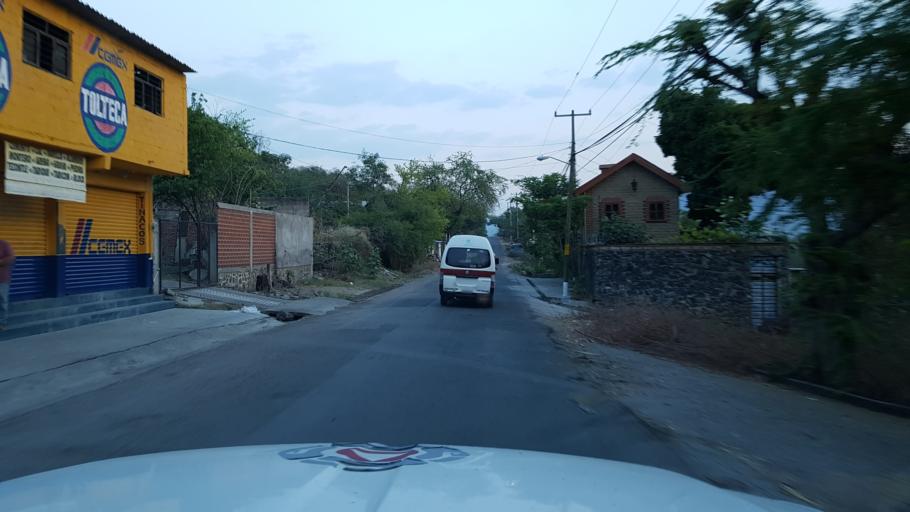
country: MX
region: Morelos
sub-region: Tlaltizapan de Zapata
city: Colonia Palo Prieto (Chipitongo)
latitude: 18.7048
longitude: -99.1064
